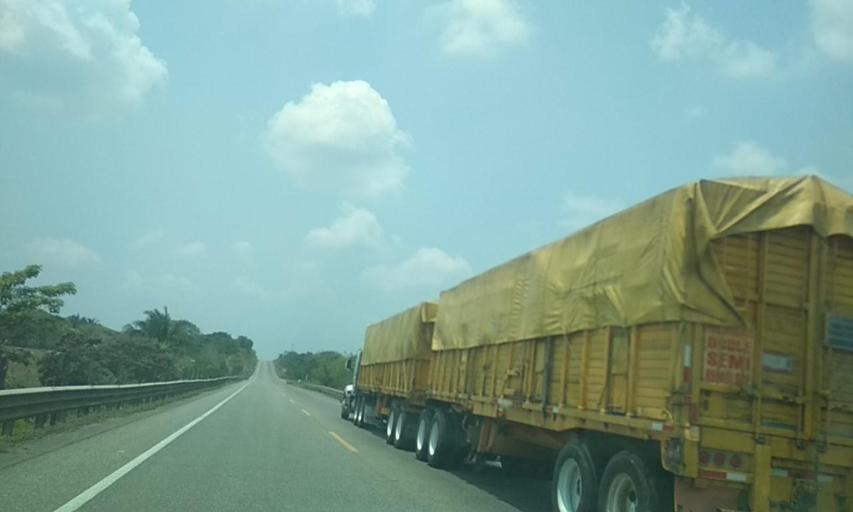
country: MX
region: Tabasco
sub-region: Huimanguillo
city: Francisco Rueda
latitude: 17.7375
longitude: -93.9773
